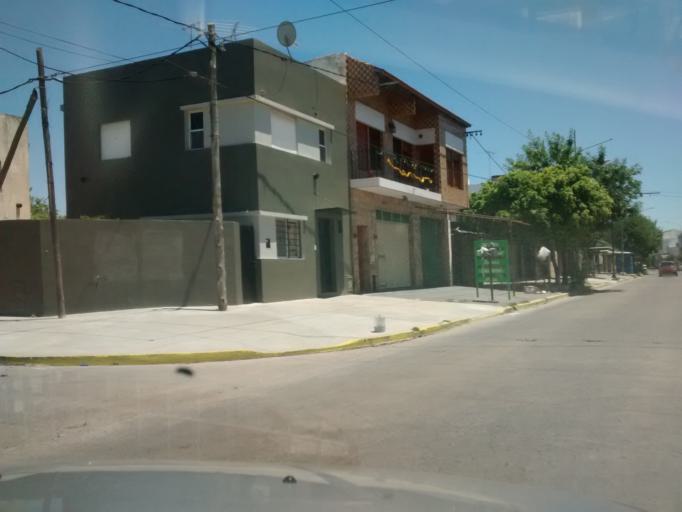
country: AR
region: Buenos Aires
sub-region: Partido de Berisso
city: Berisso
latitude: -34.8795
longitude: -57.8480
